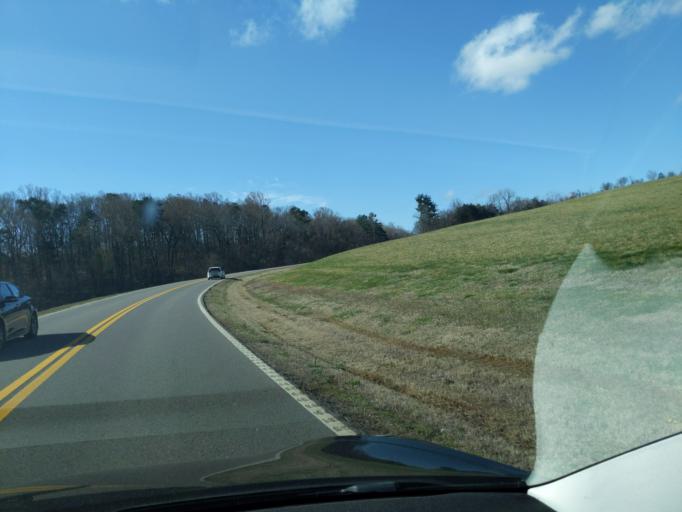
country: US
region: Tennessee
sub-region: Sevier County
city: Sevierville
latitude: 35.9701
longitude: -83.5412
